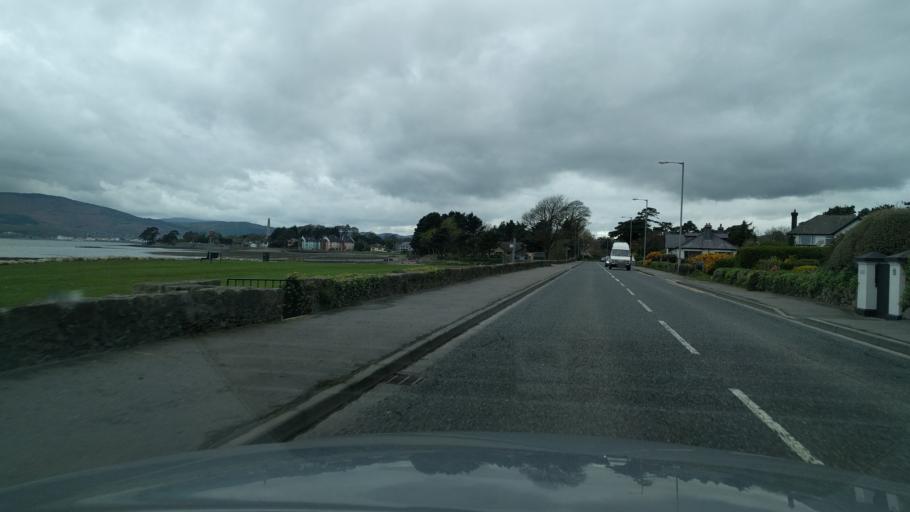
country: GB
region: Northern Ireland
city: Rostrevor
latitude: 54.0968
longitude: -6.1965
